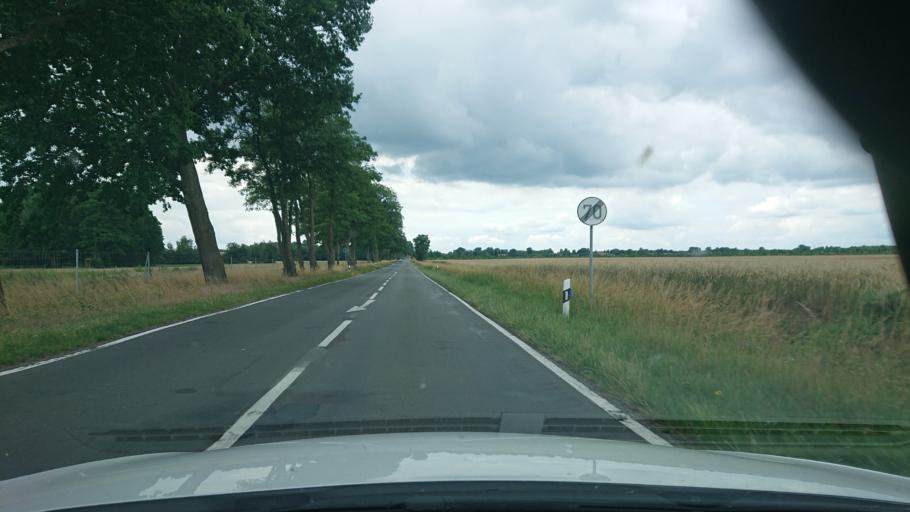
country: DE
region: Mecklenburg-Vorpommern
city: Ludwigslust
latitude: 53.3500
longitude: 11.4267
